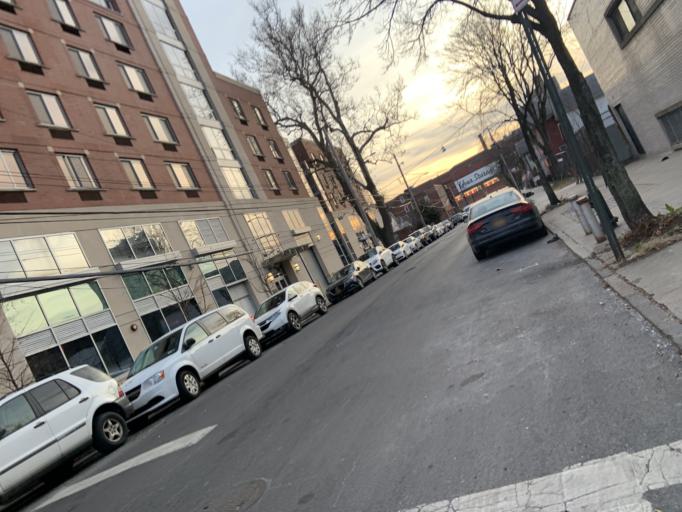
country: US
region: New York
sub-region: New York County
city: Inwood
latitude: 40.8804
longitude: -73.9078
